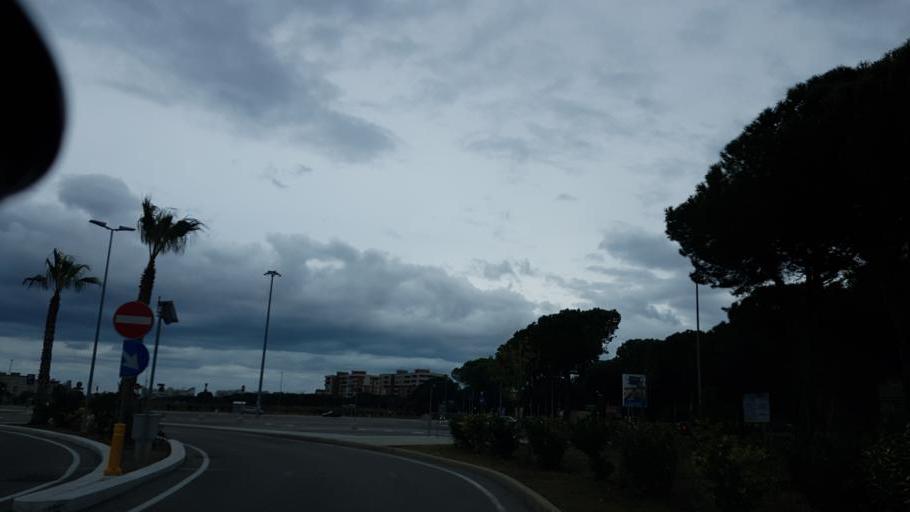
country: IT
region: Apulia
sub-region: Provincia di Brindisi
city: Brindisi
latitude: 40.6217
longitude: 17.9166
